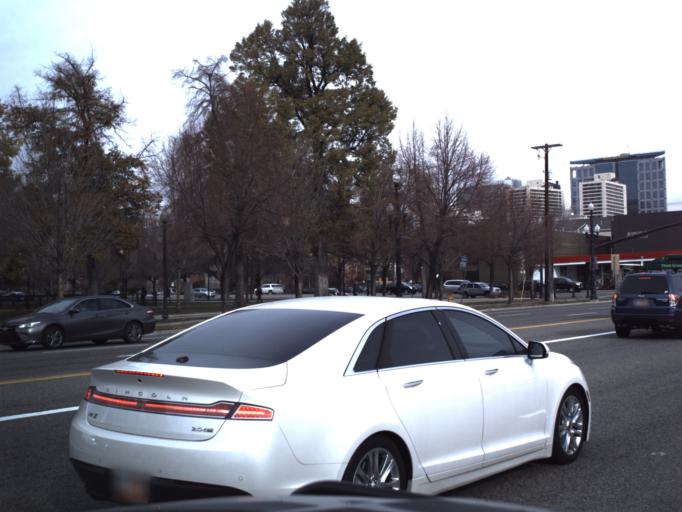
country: US
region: Utah
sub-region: Salt Lake County
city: Salt Lake City
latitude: 40.7605
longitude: -111.9009
